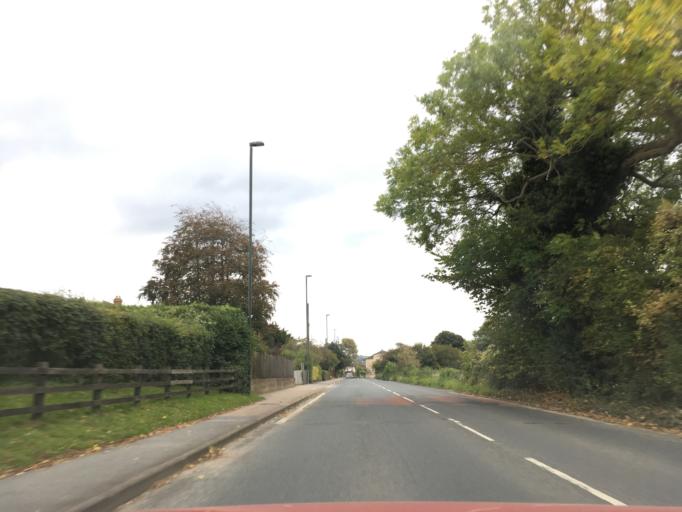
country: GB
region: England
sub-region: Gloucestershire
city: Stonehouse
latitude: 51.7408
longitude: -2.2642
